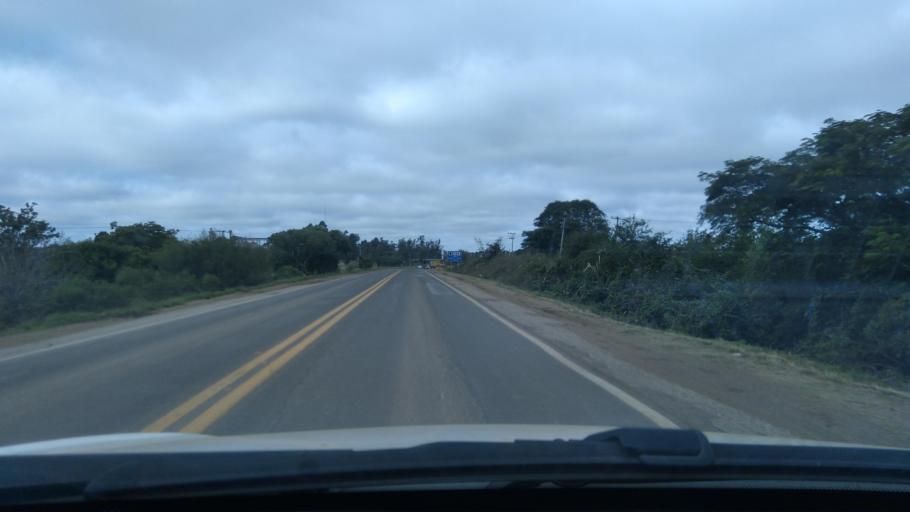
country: BR
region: Rio Grande do Sul
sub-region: Dom Pedrito
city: Dom Pedrito
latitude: -30.9729
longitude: -54.6524
